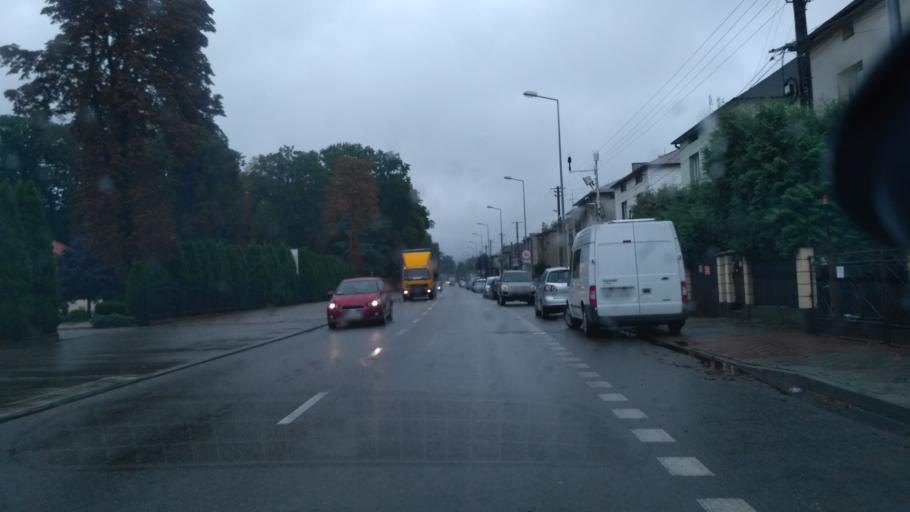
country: PL
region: Subcarpathian Voivodeship
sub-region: Powiat debicki
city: Debica
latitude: 50.0618
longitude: 21.4058
